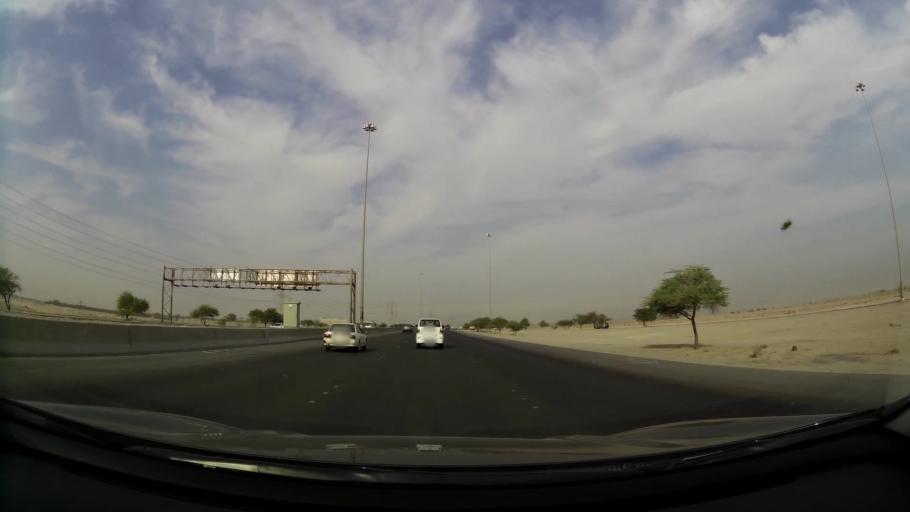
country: KW
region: Al Asimah
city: Ar Rabiyah
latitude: 29.2664
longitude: 47.8340
